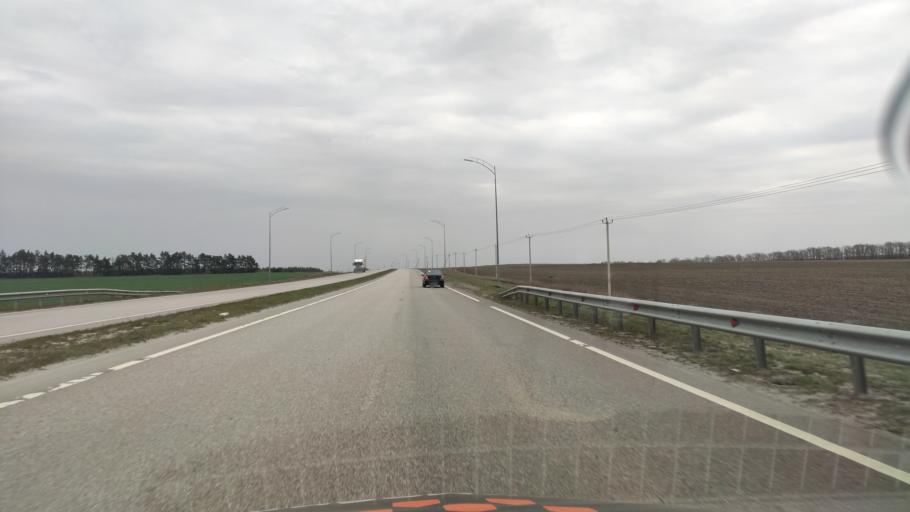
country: RU
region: Belgorod
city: Staryy Oskol
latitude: 51.3918
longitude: 37.8674
